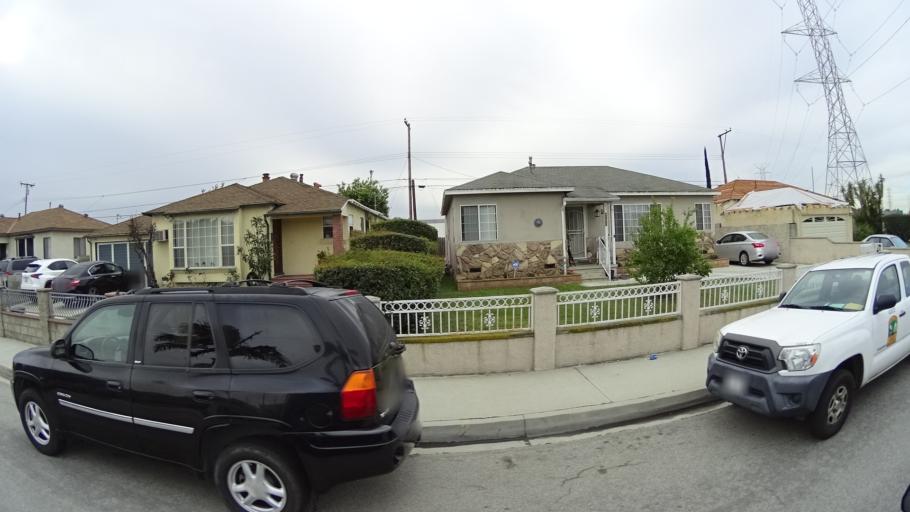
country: US
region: California
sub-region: Los Angeles County
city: Avocado Heights
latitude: 34.0622
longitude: -117.9976
